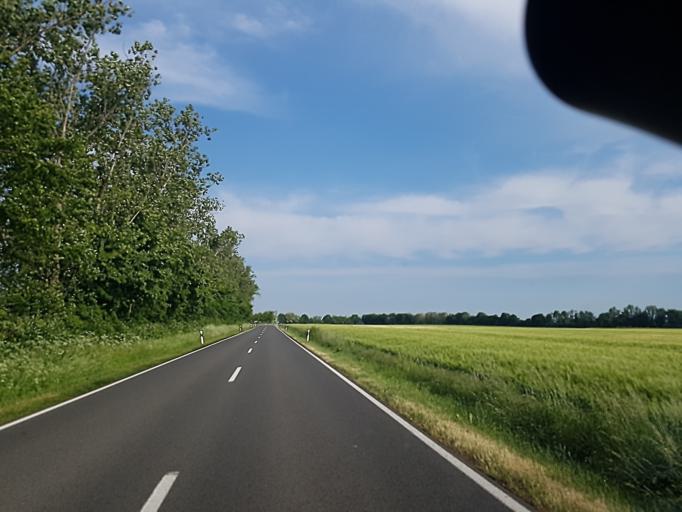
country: DE
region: Saxony-Anhalt
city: Kropstadt
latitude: 52.0154
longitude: 12.7547
